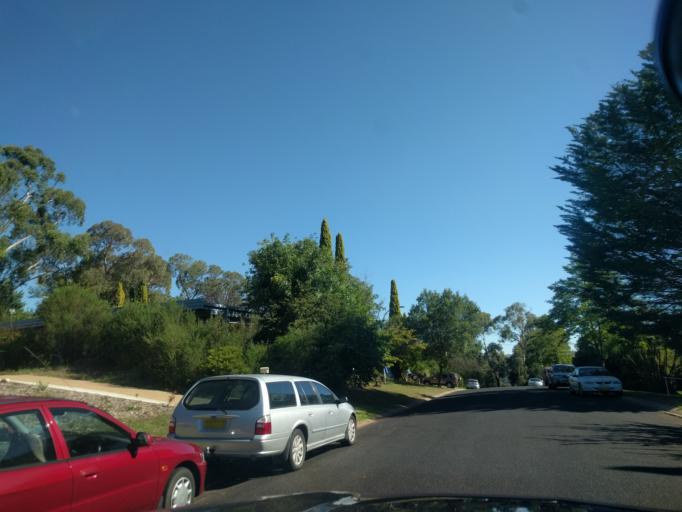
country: AU
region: New South Wales
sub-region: Armidale Dumaresq
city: Armidale
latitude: -30.4991
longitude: 151.6622
